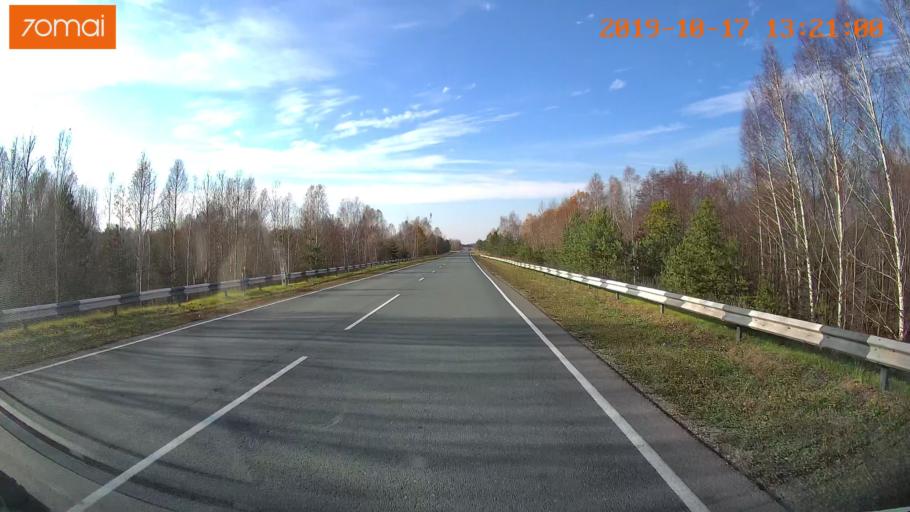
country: RU
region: Rjazan
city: Gus'-Zheleznyy
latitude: 55.0793
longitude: 41.0377
